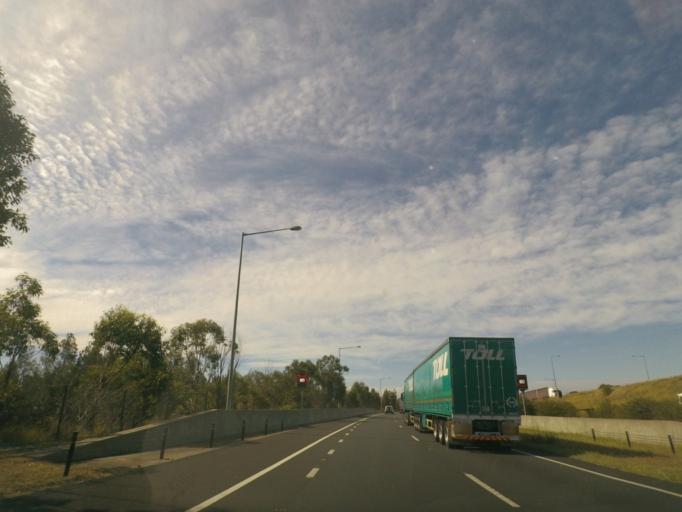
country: AU
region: New South Wales
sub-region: Liverpool
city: Miller
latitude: -33.9488
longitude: 150.8770
